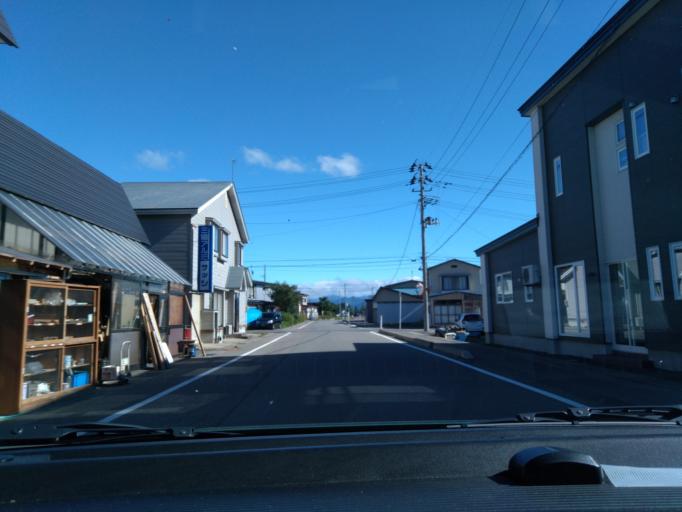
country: JP
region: Akita
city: Yuzawa
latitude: 39.2028
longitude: 140.5513
